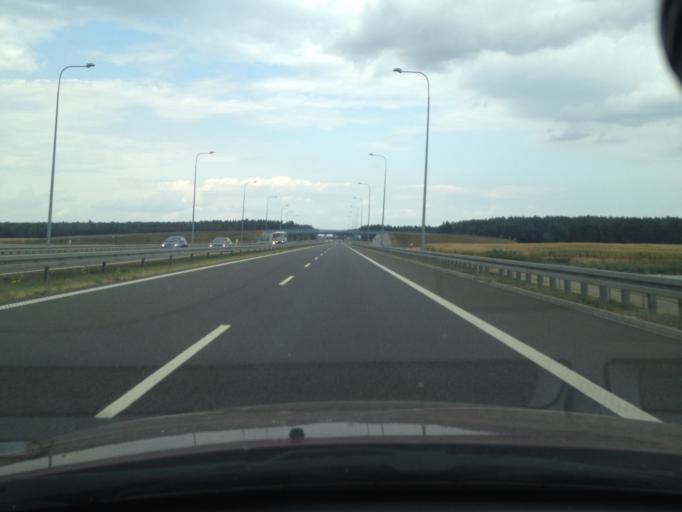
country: PL
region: West Pomeranian Voivodeship
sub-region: Powiat pyrzycki
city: Bielice
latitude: 53.1457
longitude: 14.7167
